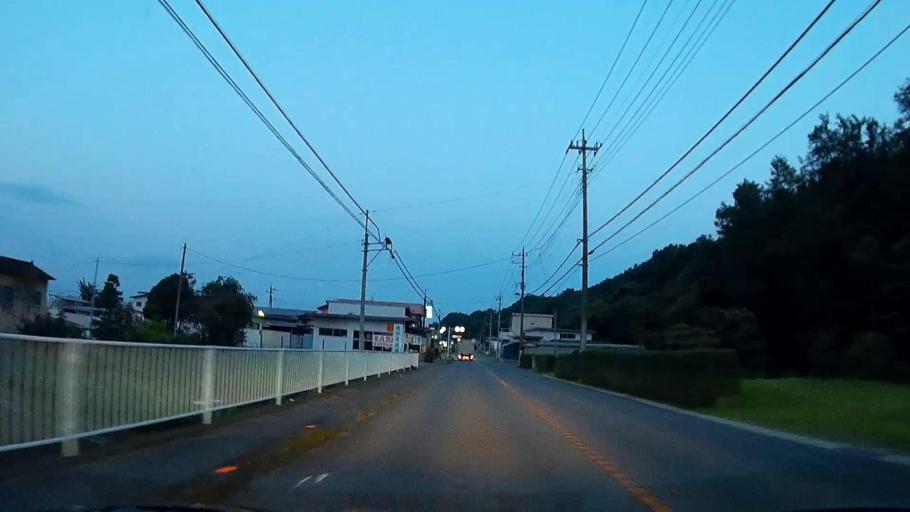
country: JP
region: Gunma
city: Annaka
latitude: 36.3526
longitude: 138.9355
